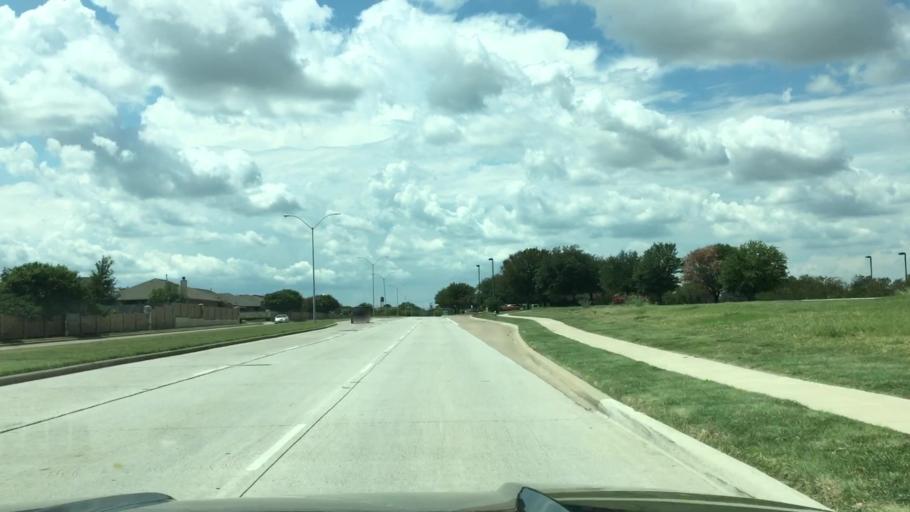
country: US
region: Texas
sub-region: Tarrant County
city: Blue Mound
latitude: 32.8614
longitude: -97.3279
